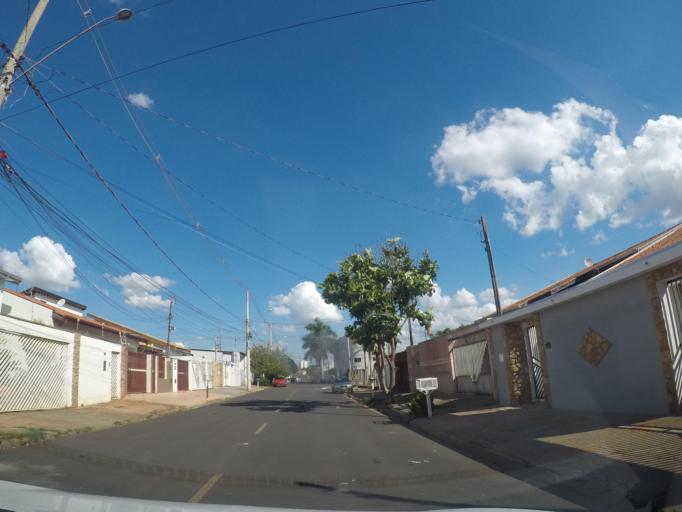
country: BR
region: Sao Paulo
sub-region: Sumare
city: Sumare
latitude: -22.8311
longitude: -47.2801
